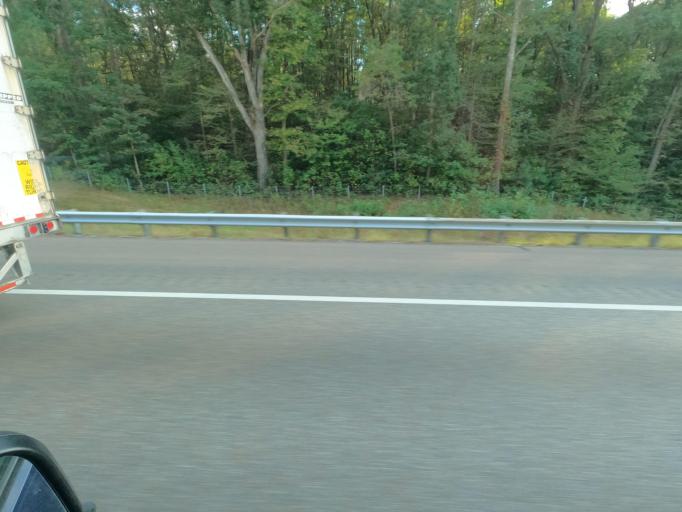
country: US
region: Tennessee
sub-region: Decatur County
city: Parsons
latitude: 35.8184
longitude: -88.2574
